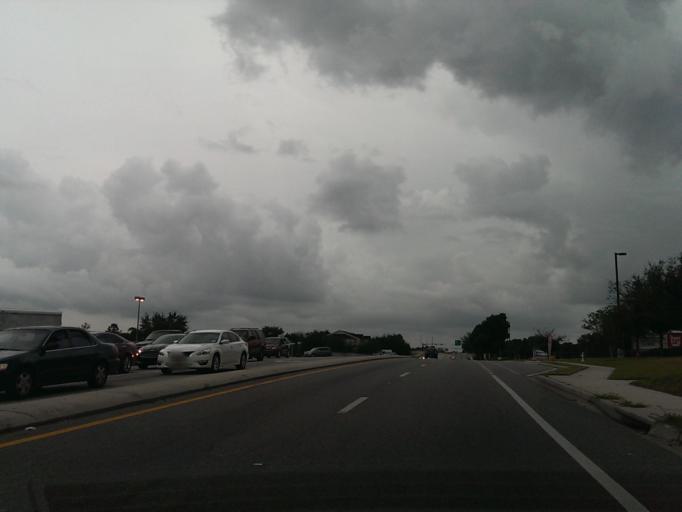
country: US
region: Florida
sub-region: Orange County
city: Gotha
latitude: 28.5517
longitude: -81.5050
